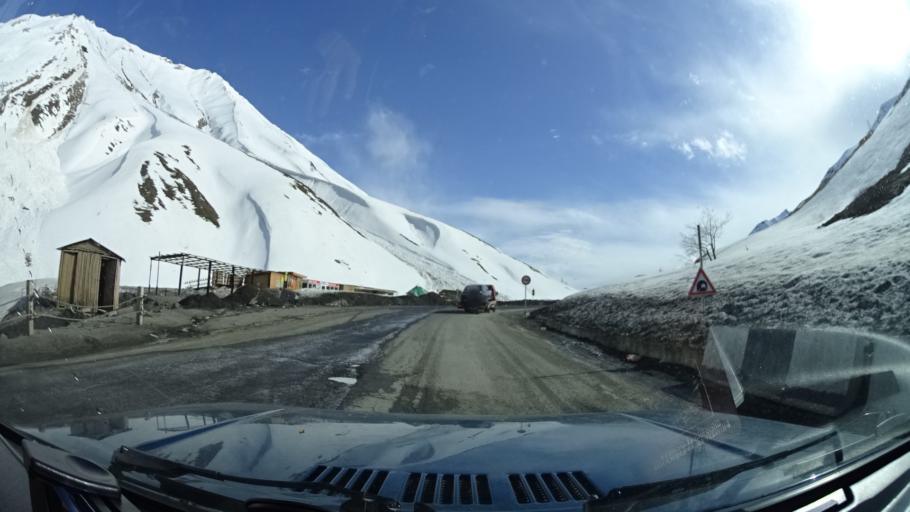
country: GE
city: Gudauri
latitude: 42.5323
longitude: 44.4724
